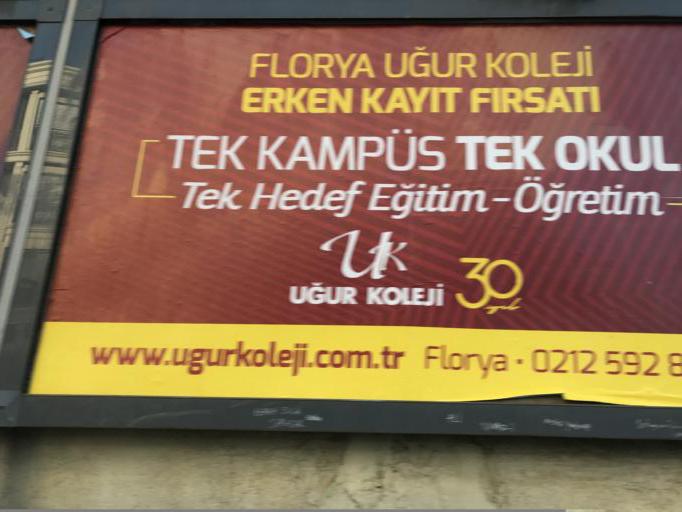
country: TR
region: Istanbul
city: Bahcelievler
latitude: 40.9626
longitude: 28.8188
